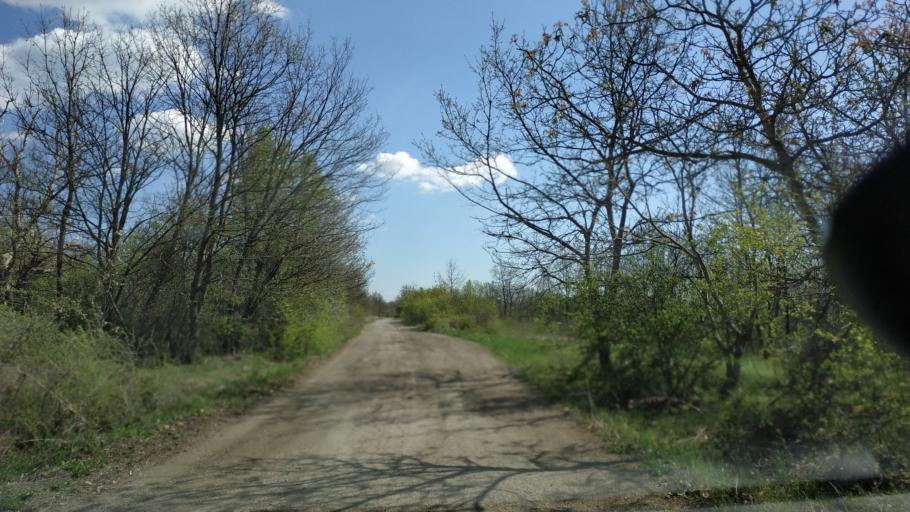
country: RS
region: Central Serbia
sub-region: Zajecarski Okrug
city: Soko Banja
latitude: 43.5334
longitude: 21.9061
